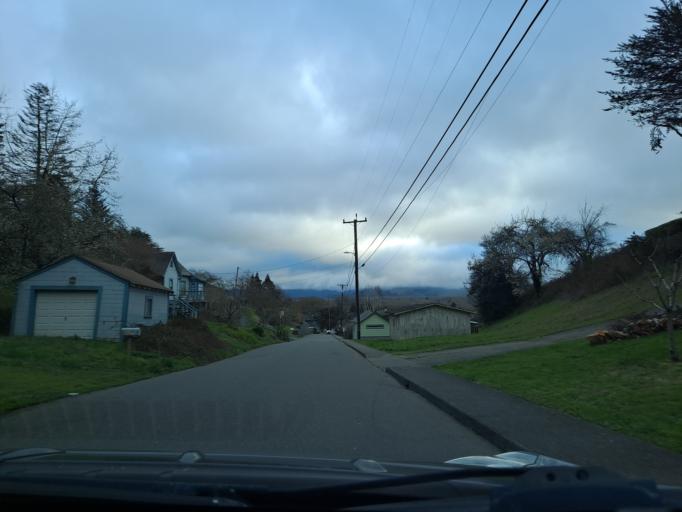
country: US
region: California
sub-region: Humboldt County
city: Fortuna
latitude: 40.6017
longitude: -124.1609
